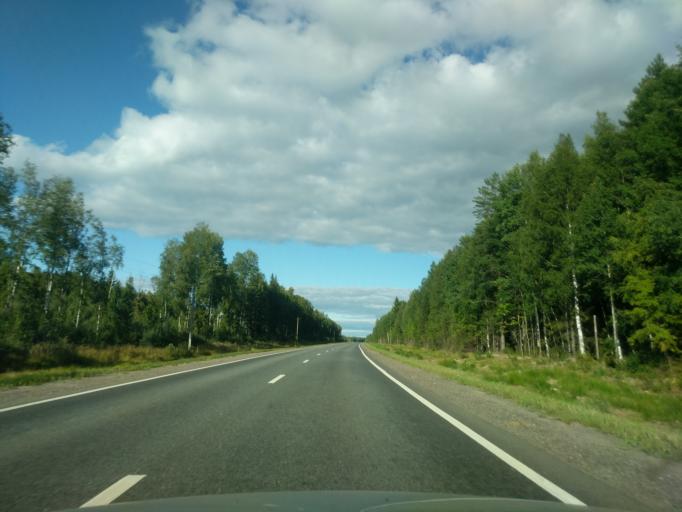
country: RU
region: Kostroma
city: Manturovo
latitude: 58.1539
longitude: 44.3791
